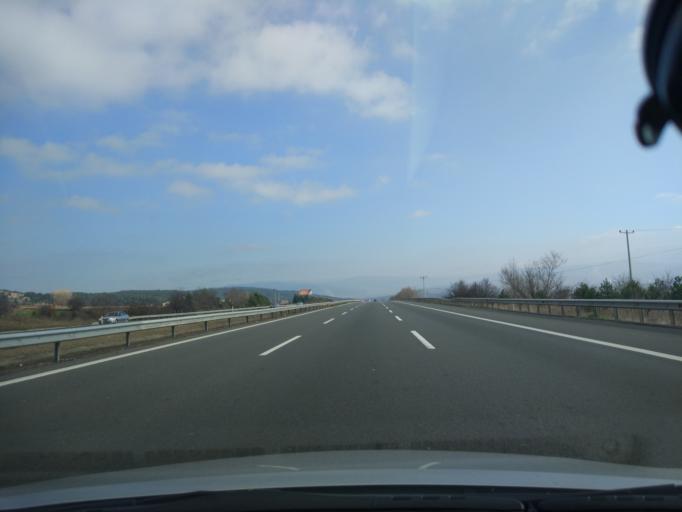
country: TR
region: Bolu
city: Bolu
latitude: 40.7770
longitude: 31.6923
